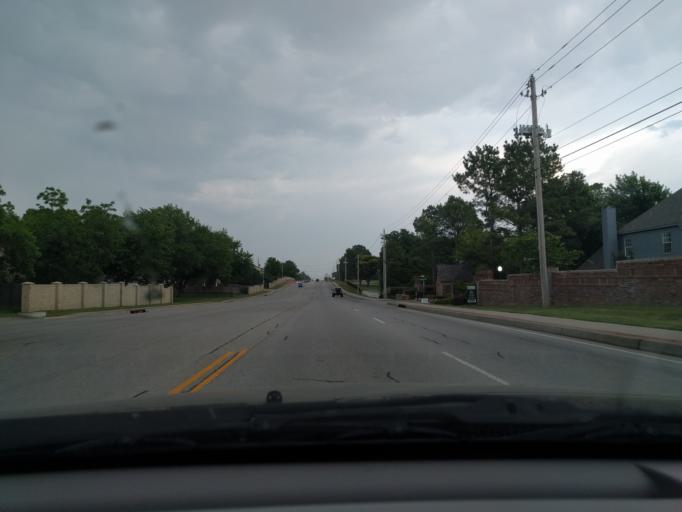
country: US
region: Oklahoma
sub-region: Tulsa County
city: Broken Arrow
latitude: 36.0463
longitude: -95.8806
